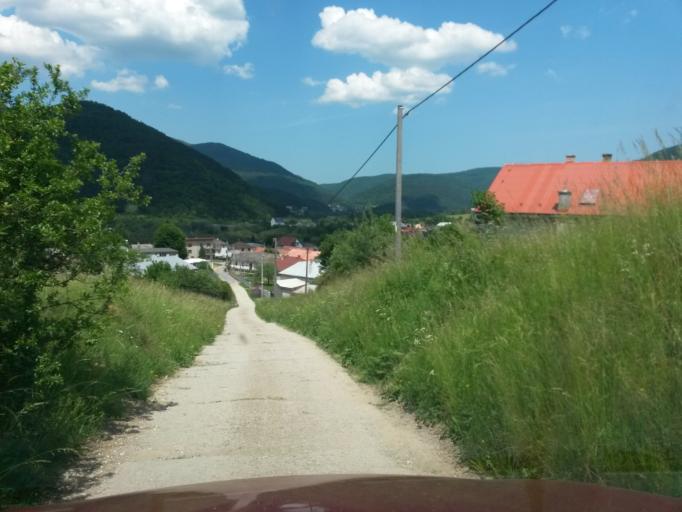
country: SK
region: Kosicky
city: Gelnica
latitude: 48.8690
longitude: 20.9882
